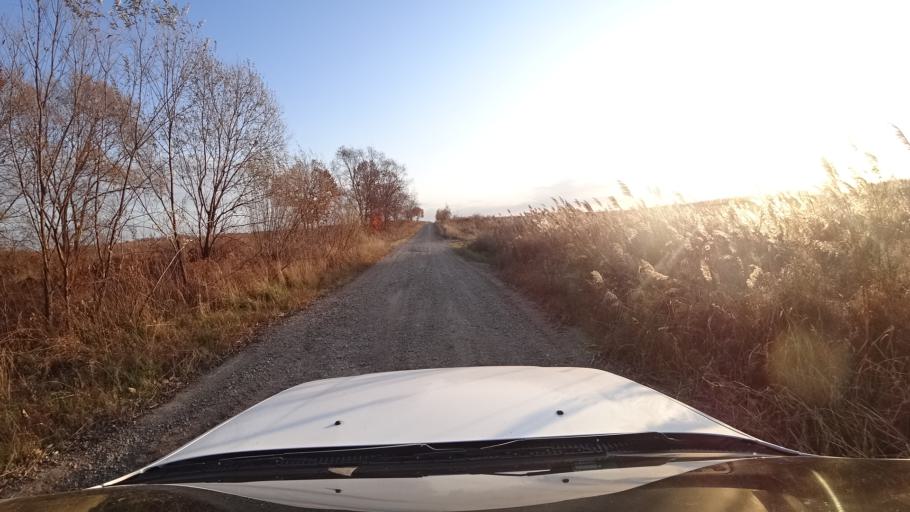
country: RU
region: Primorskiy
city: Lazo
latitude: 45.8143
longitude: 133.6101
